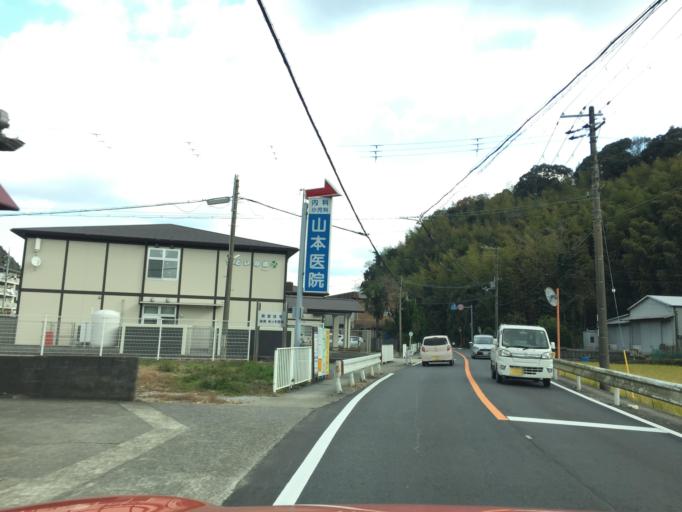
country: JP
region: Wakayama
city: Kainan
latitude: 34.1727
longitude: 135.2421
